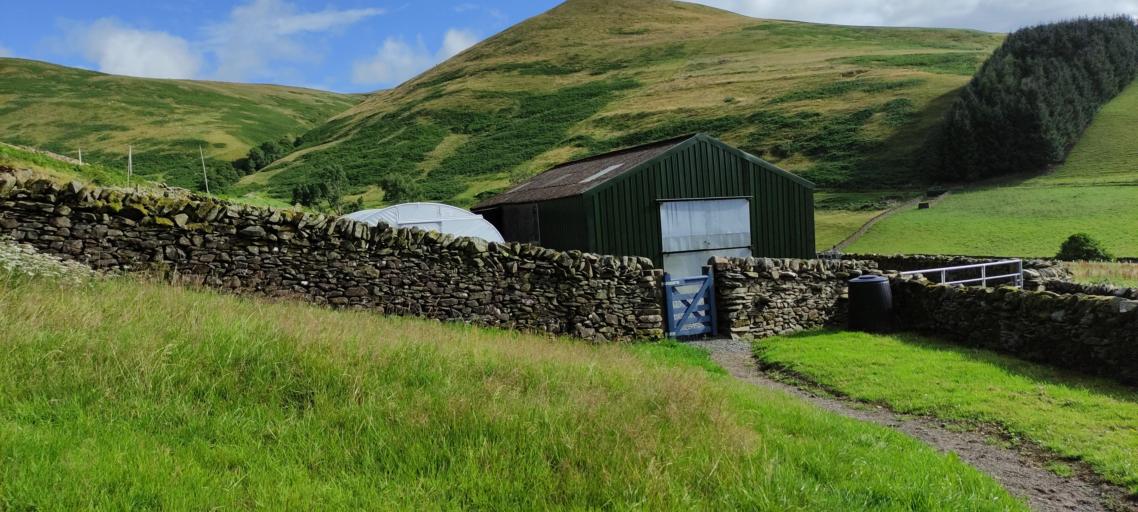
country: GB
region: Scotland
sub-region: Dumfries and Galloway
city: Langholm
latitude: 55.2287
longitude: -2.9905
